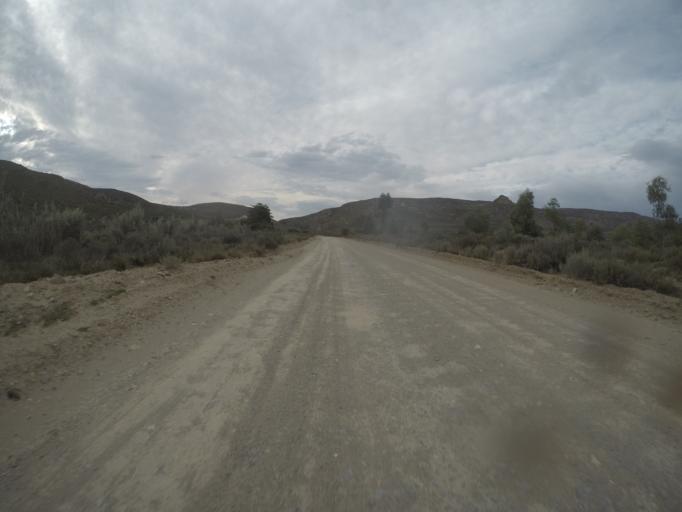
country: ZA
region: Eastern Cape
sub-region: Cacadu District Municipality
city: Willowmore
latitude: -33.4995
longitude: 23.6371
